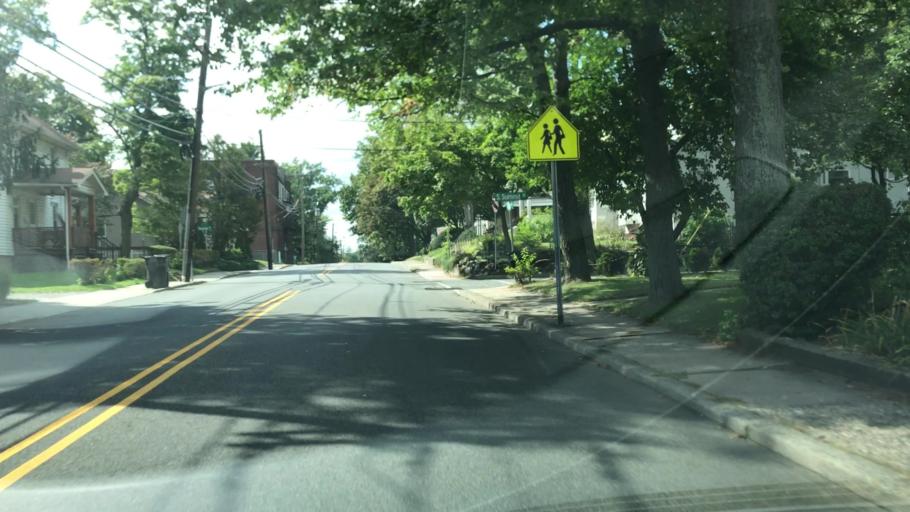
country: US
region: New Jersey
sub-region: Bergen County
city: Bergenfield
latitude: 40.9239
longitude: -73.9928
